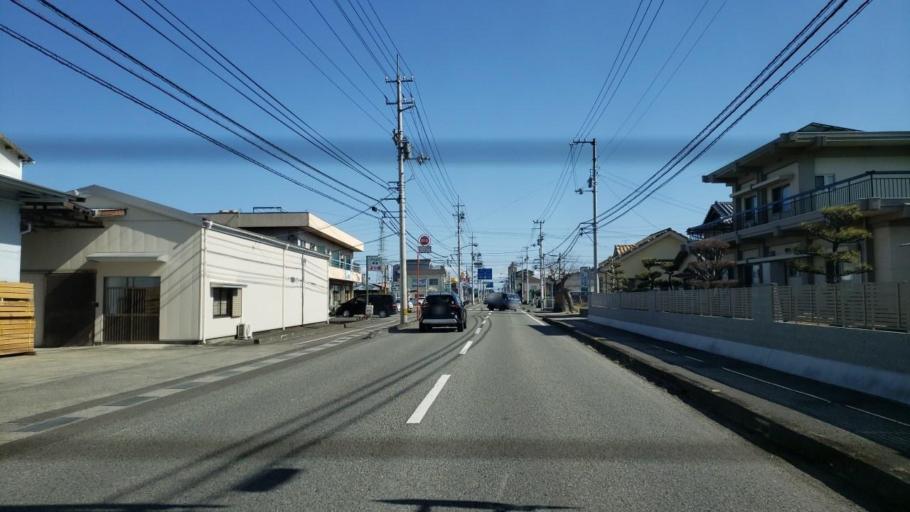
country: JP
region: Tokushima
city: Tokushima-shi
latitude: 34.1329
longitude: 134.5158
